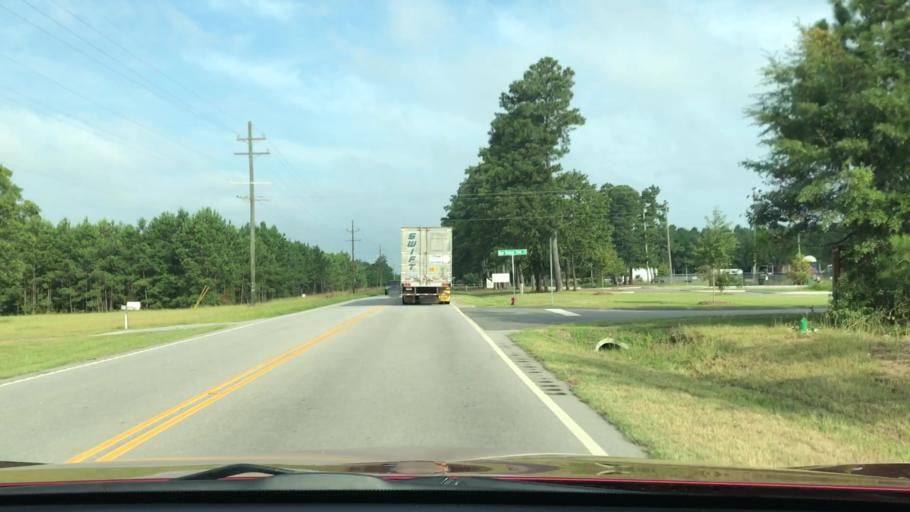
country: US
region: South Carolina
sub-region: Barnwell County
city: Williston
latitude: 33.6414
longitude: -81.3366
